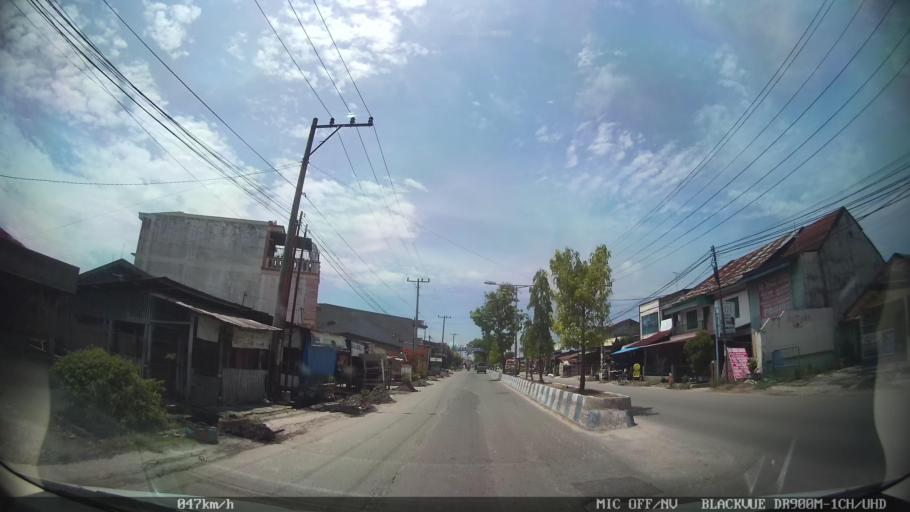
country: ID
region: North Sumatra
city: Percut
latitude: 3.5531
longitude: 98.8795
